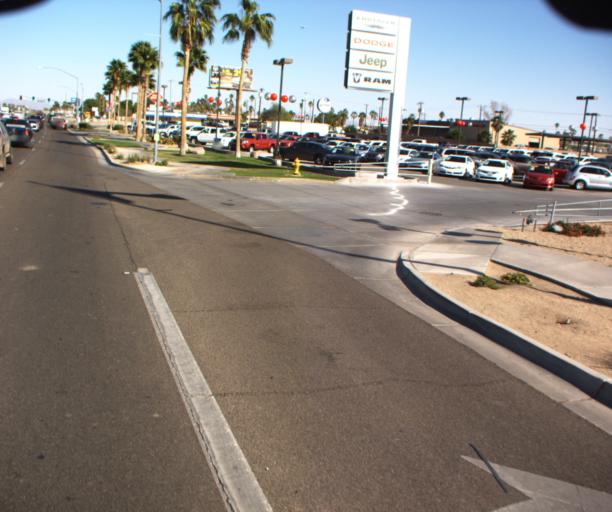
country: US
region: Arizona
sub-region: Yuma County
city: Yuma
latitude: 32.6693
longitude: -114.6183
